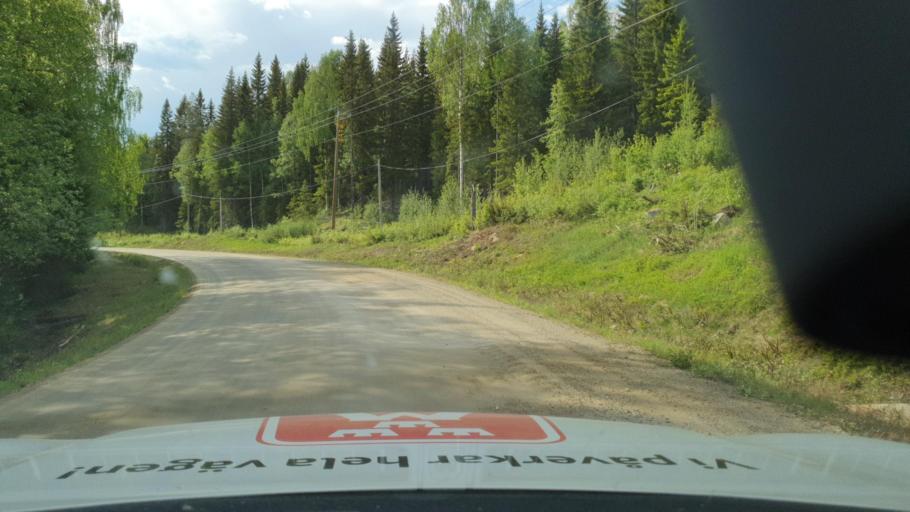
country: SE
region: Vaesterbotten
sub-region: Vindelns Kommun
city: Vindeln
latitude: 64.0933
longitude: 19.7168
